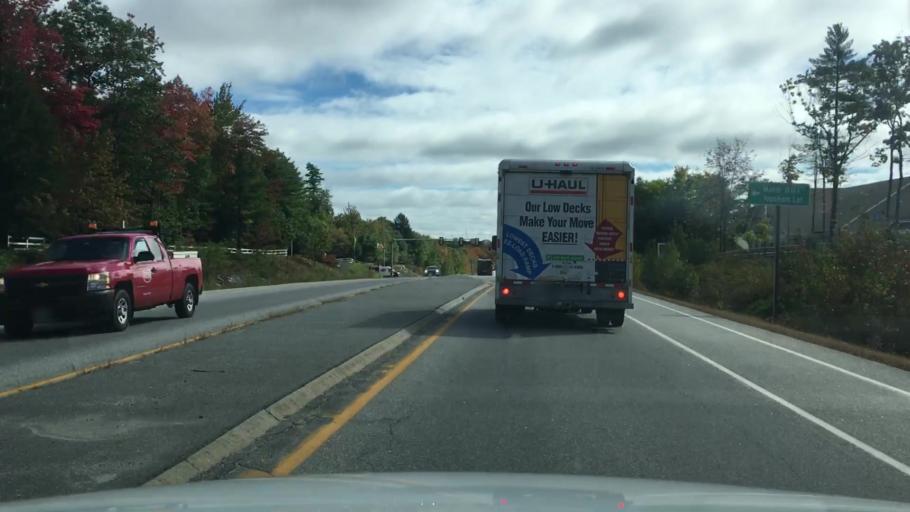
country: US
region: Maine
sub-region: Sagadahoc County
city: Topsham
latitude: 43.9365
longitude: -69.9585
